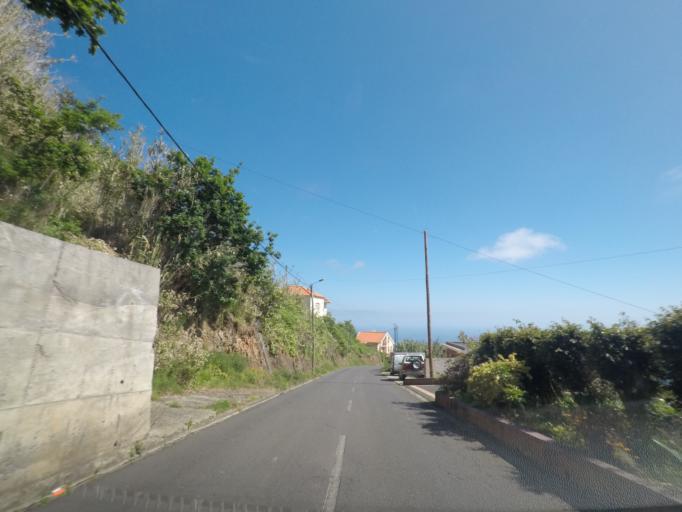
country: PT
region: Madeira
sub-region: Calheta
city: Arco da Calheta
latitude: 32.7042
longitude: -17.1120
